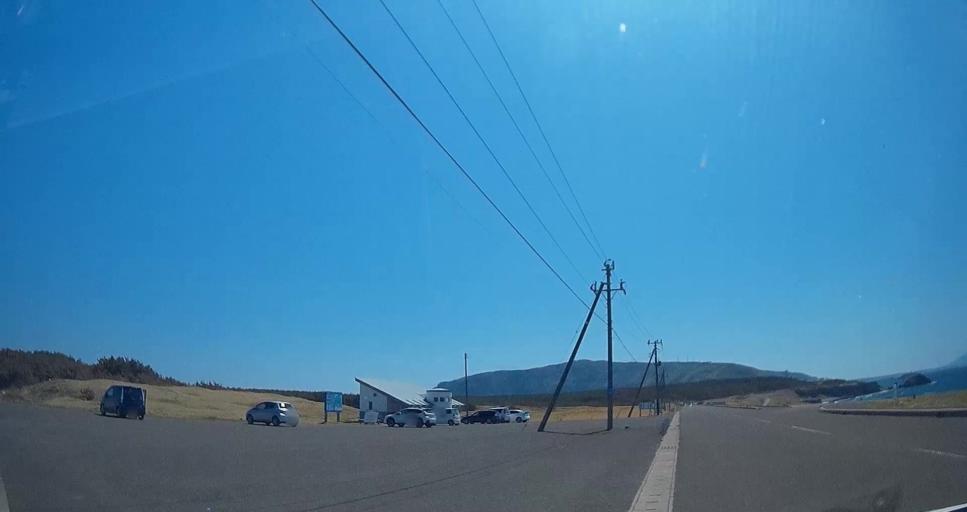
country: JP
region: Aomori
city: Mutsu
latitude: 41.4280
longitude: 141.4599
